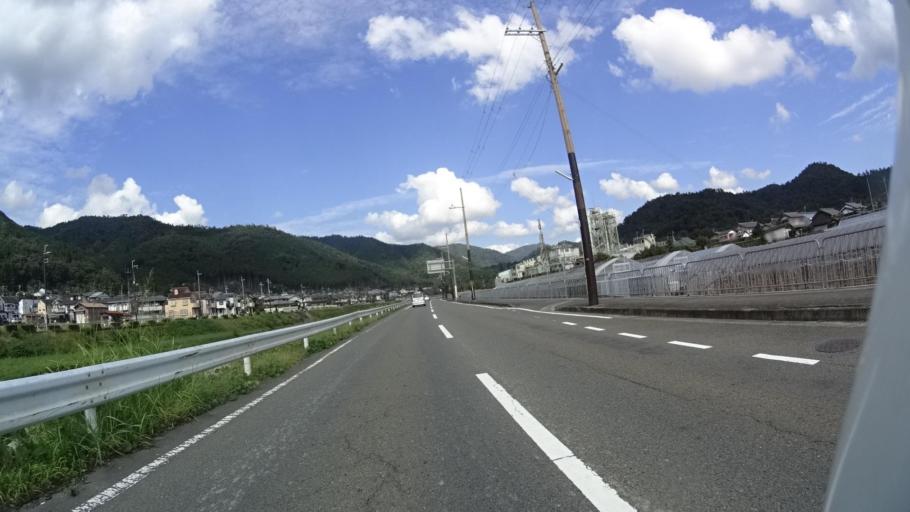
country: JP
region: Kyoto
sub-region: Kyoto-shi
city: Kamigyo-ku
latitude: 35.0712
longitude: 135.7426
